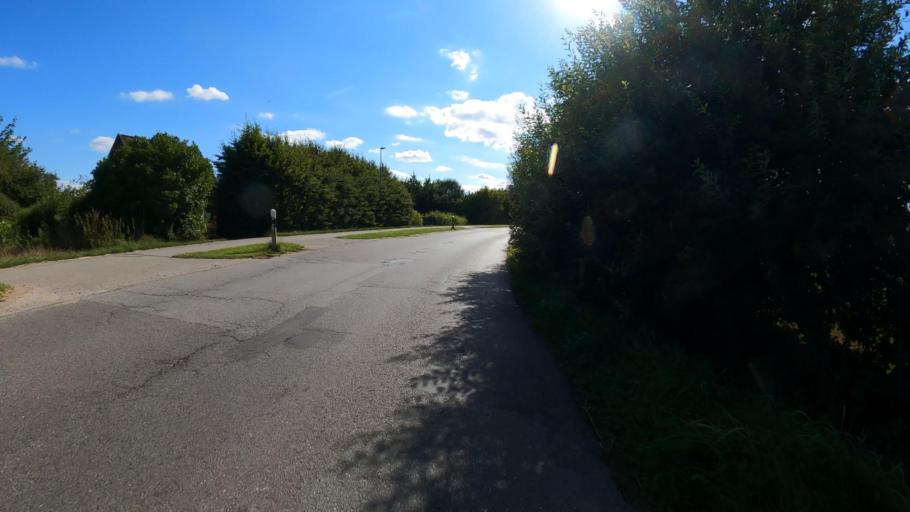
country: DE
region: Schleswig-Holstein
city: Todendorf
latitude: 53.7032
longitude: 10.3762
